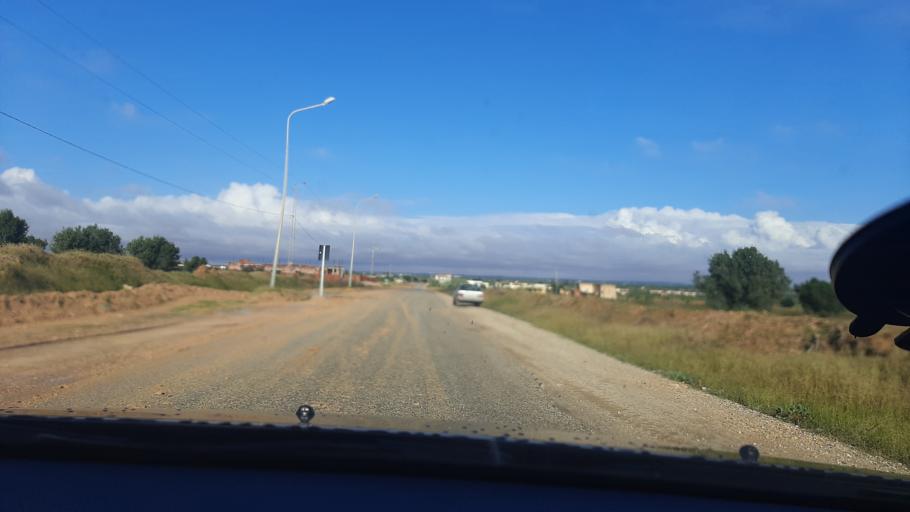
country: TN
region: Safaqis
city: Sfax
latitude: 34.8821
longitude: 10.6310
